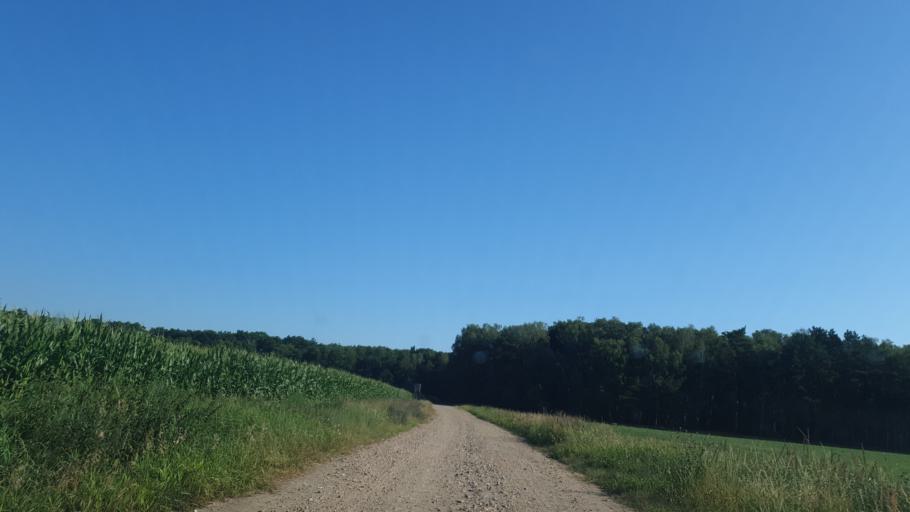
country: DE
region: Mecklenburg-Vorpommern
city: Torgelow
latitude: 53.6506
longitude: 13.9517
